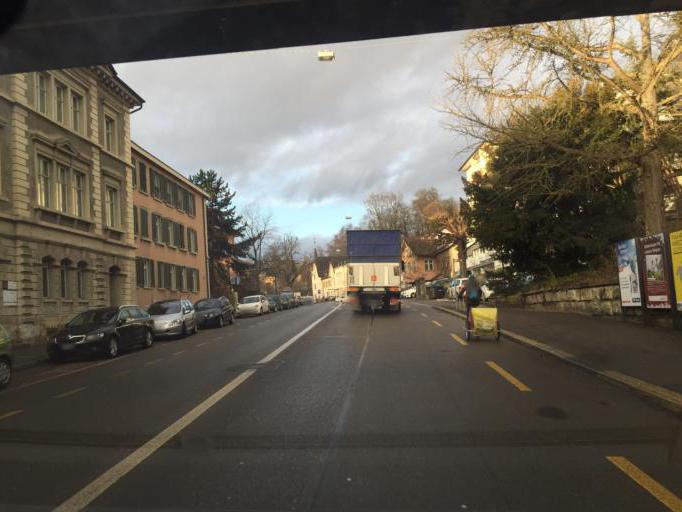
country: CH
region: Schaffhausen
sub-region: Bezirk Schaffhausen
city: Schaffhausen
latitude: 47.6970
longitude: 8.6378
